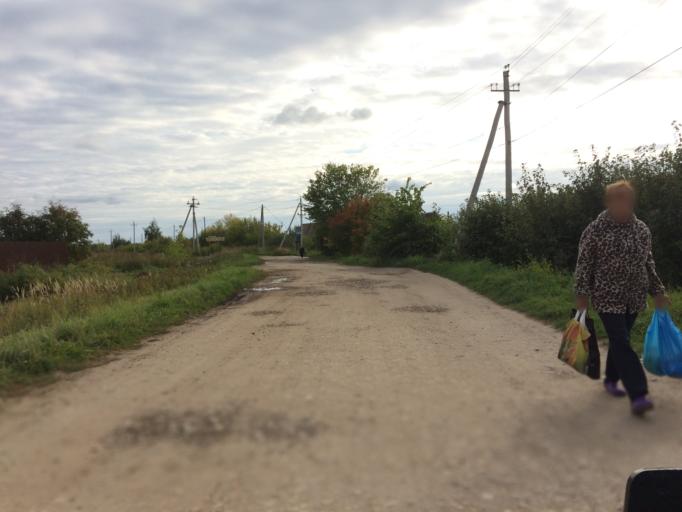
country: RU
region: Mariy-El
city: Yoshkar-Ola
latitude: 56.6557
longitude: 48.0043
